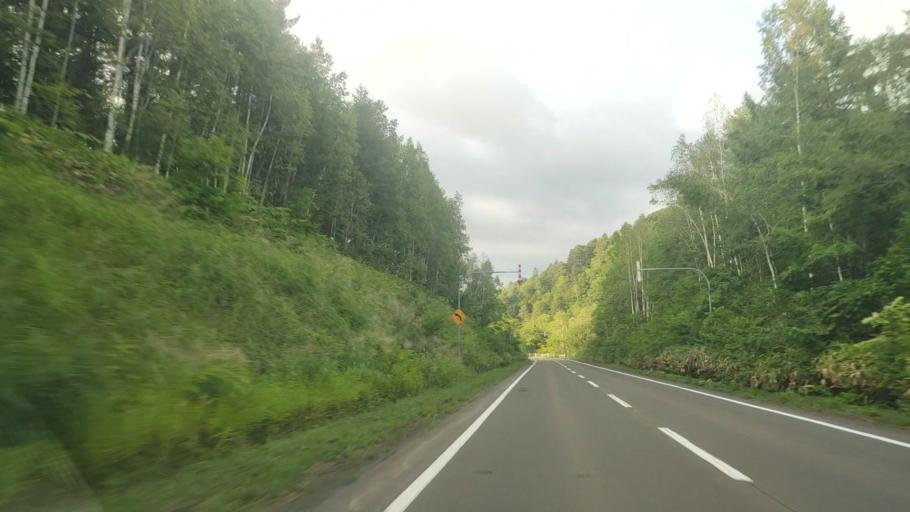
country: JP
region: Hokkaido
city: Bibai
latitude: 43.1364
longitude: 142.0960
